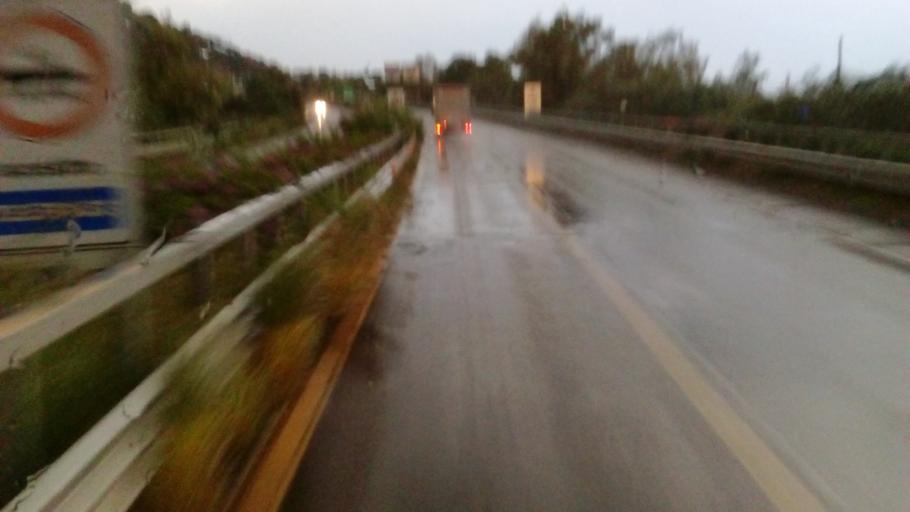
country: IT
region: Sicily
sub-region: Messina
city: Larderia
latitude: 38.1193
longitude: 15.5143
